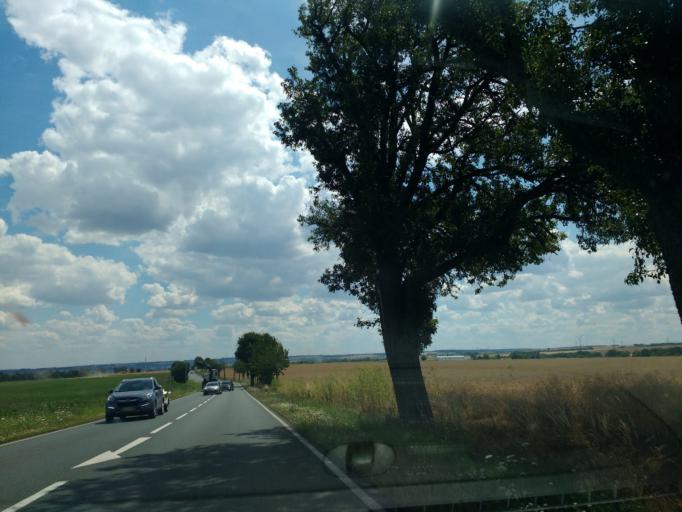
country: DE
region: Saxony-Anhalt
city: Droyssig
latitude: 51.0732
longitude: 12.0360
